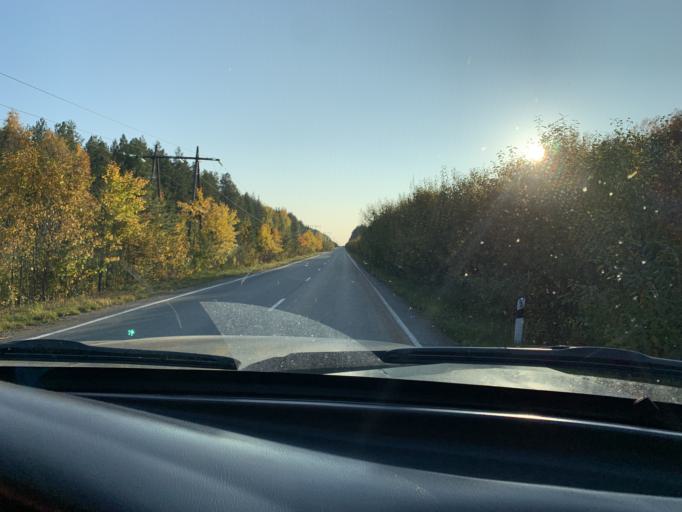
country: RU
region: Sverdlovsk
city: Verkhneye Dubrovo
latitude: 56.8750
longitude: 61.1106
